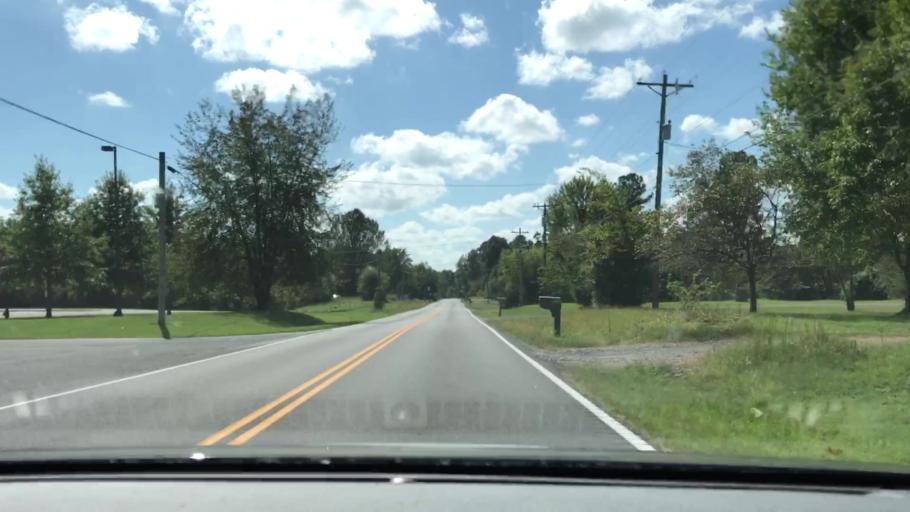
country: US
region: Kentucky
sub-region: McCracken County
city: Reidland
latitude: 36.9165
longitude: -88.5207
